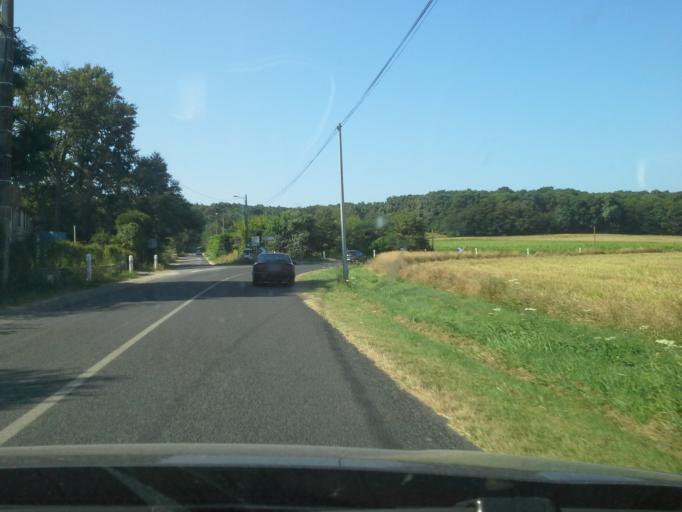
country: FR
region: Centre
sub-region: Departement du Loir-et-Cher
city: Cande-sur-Beuvron
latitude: 47.4913
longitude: 1.2589
